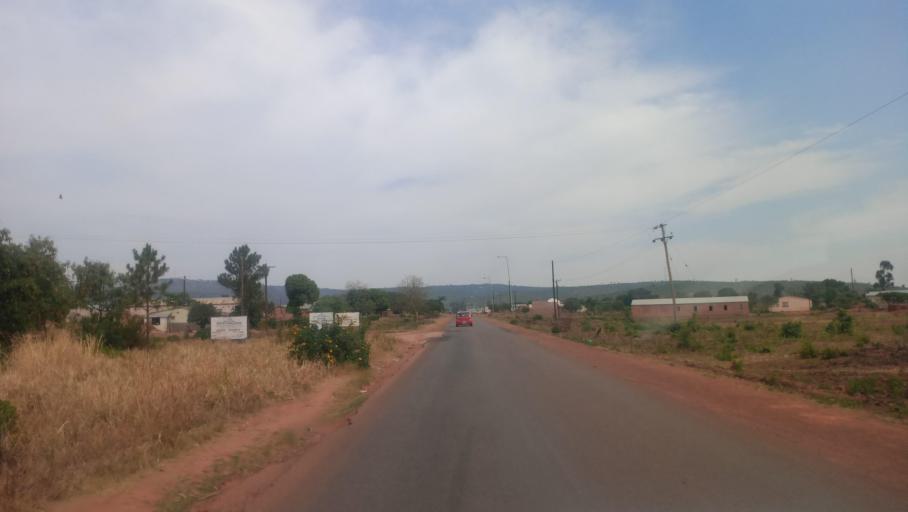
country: ZM
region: Northern
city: Mpika
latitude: -11.8402
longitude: 31.4367
